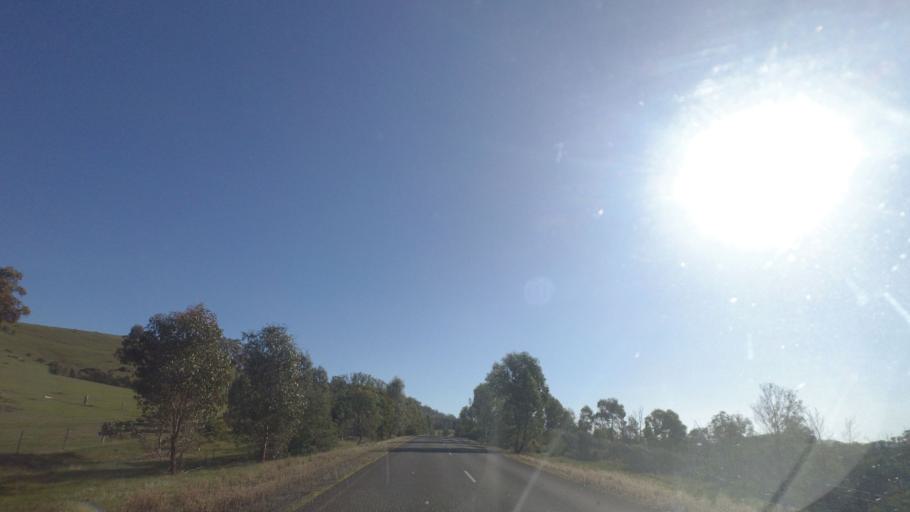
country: AU
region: Victoria
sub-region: Mount Alexander
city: Castlemaine
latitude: -37.0443
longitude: 144.2818
